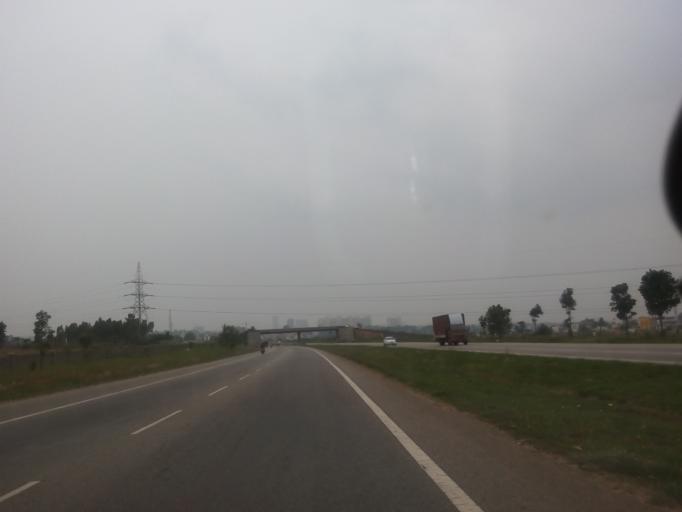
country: IN
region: Karnataka
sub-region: Bangalore Urban
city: Bangalore
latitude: 12.8659
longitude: 77.6406
